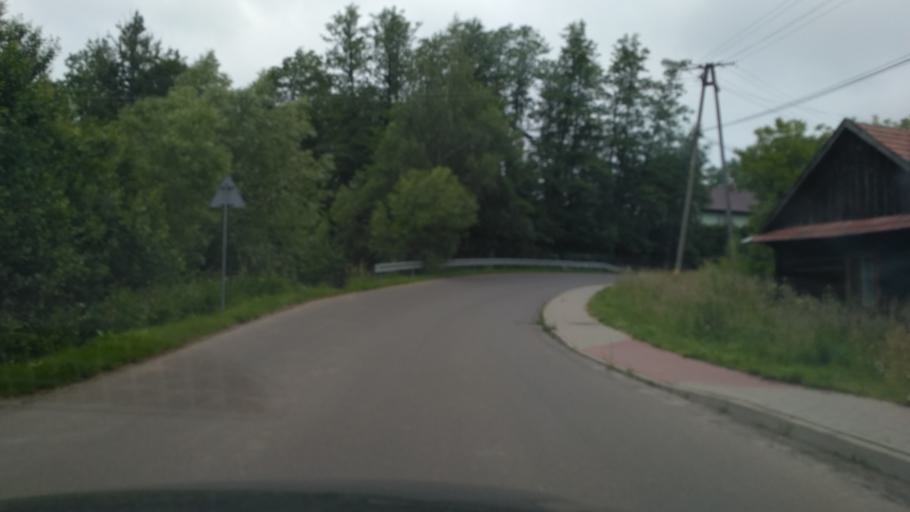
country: PL
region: Subcarpathian Voivodeship
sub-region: Powiat ropczycko-sedziszowski
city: Zagorzyce
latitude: 50.0311
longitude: 21.6869
